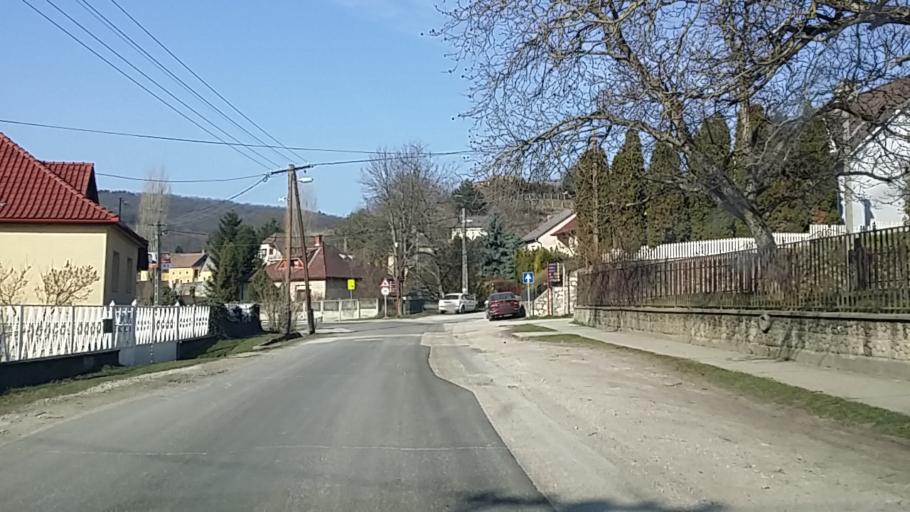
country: HU
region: Komarom-Esztergom
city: Tat
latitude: 47.7284
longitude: 18.6045
